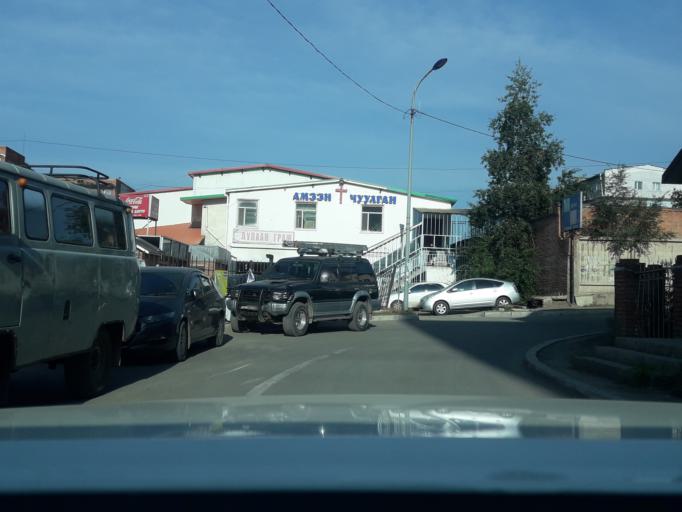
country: MN
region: Ulaanbaatar
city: Ulaanbaatar
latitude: 47.9215
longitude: 106.9476
